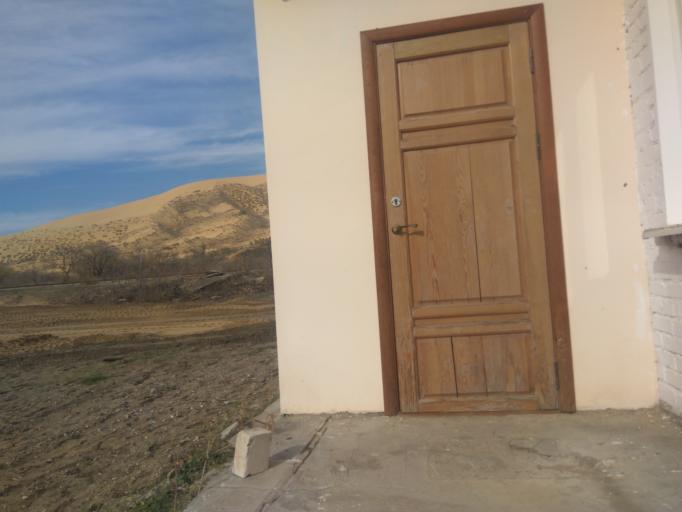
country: RU
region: Dagestan
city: Korkmaskala
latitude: 43.0024
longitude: 47.2374
